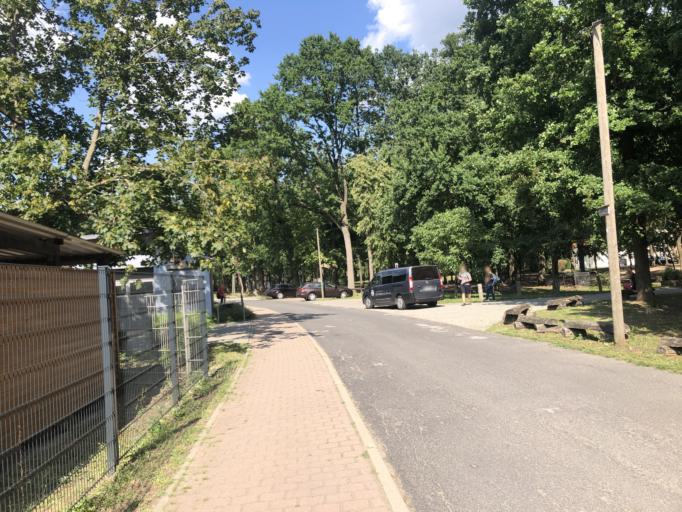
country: DE
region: Brandenburg
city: Mullrose
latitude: 52.2393
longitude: 14.4095
